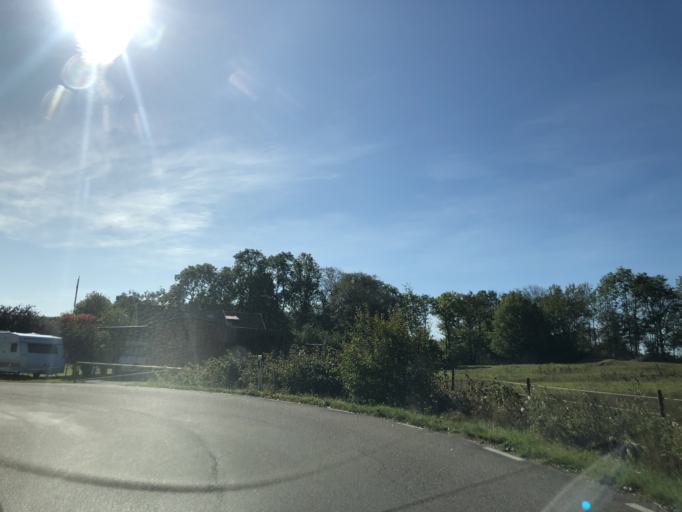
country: SE
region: Vaestra Goetaland
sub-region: Goteborg
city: Majorna
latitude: 57.7743
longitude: 11.9102
